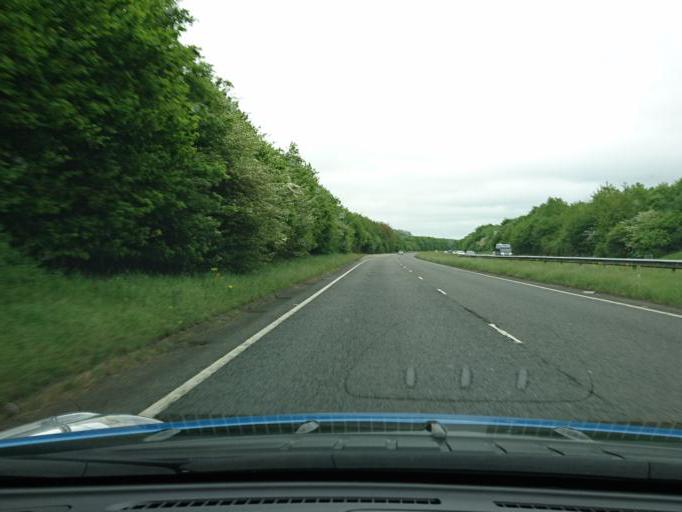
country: GB
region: England
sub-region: Oxfordshire
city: Grove
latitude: 51.6797
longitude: -1.4394
